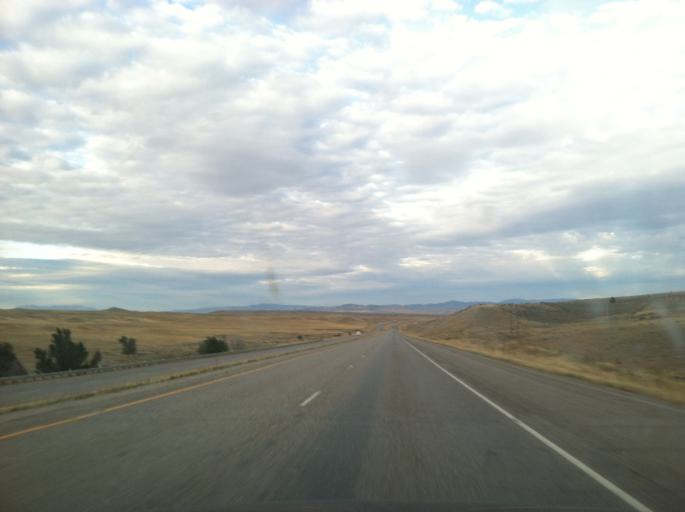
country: US
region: Montana
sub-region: Gallatin County
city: Three Forks
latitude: 45.9023
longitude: -111.8110
